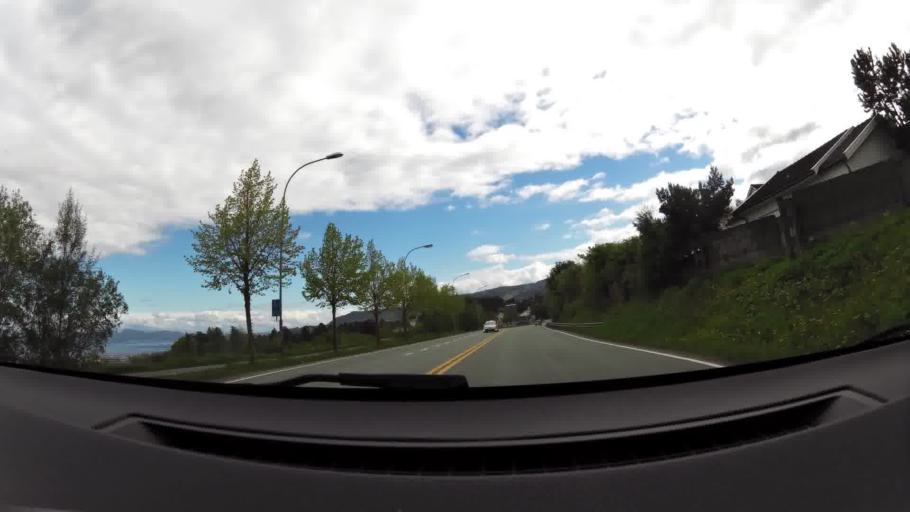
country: NO
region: Sor-Trondelag
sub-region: Trondheim
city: Trondheim
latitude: 63.4302
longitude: 10.4902
